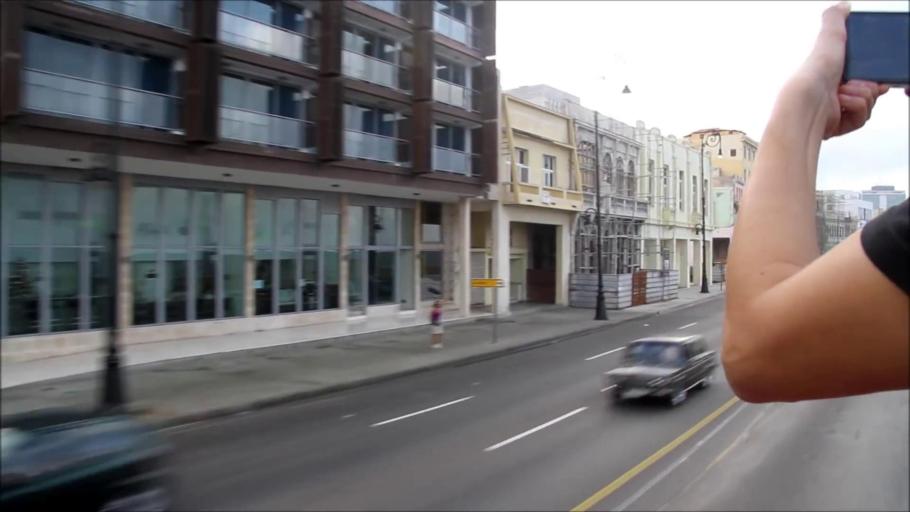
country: CU
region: La Habana
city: Centro Habana
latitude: 23.1418
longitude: -82.3678
